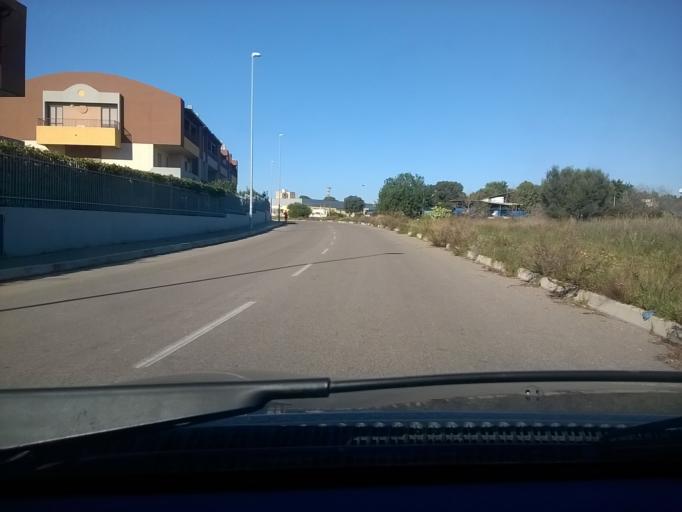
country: IT
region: Apulia
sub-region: Provincia di Taranto
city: Paolo VI
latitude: 40.5170
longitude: 17.2858
